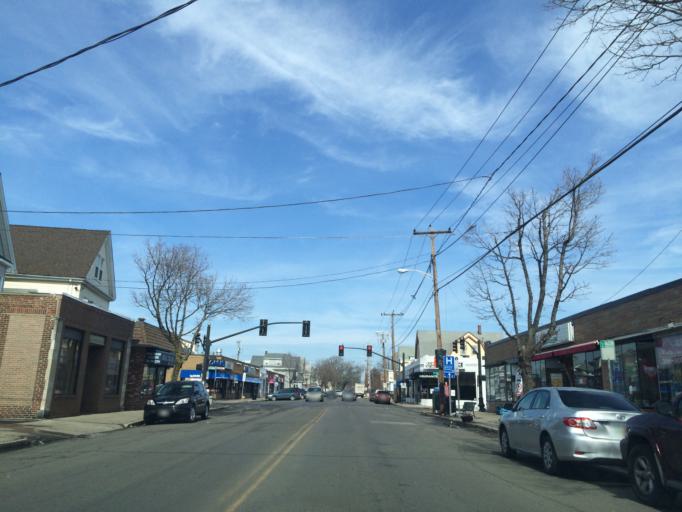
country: US
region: Massachusetts
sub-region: Middlesex County
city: Medford
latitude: 42.4046
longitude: -71.1077
